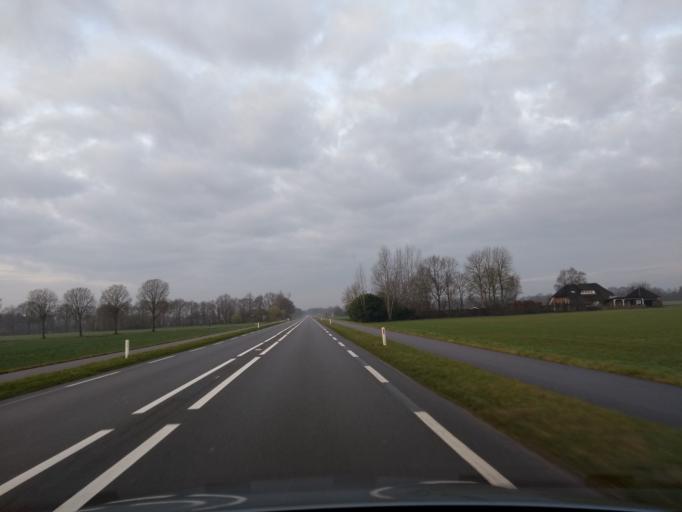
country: NL
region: Gelderland
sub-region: Gemeente Lochem
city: Laren
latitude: 52.2784
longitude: 6.3793
